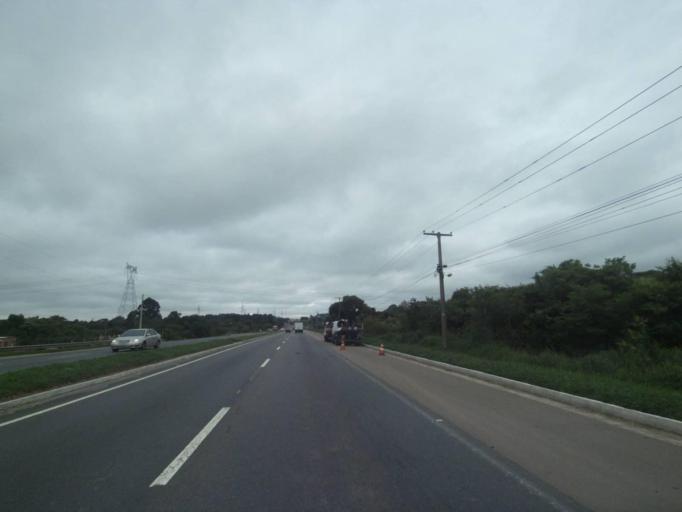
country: BR
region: Parana
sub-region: Araucaria
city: Araucaria
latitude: -25.5555
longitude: -49.3416
